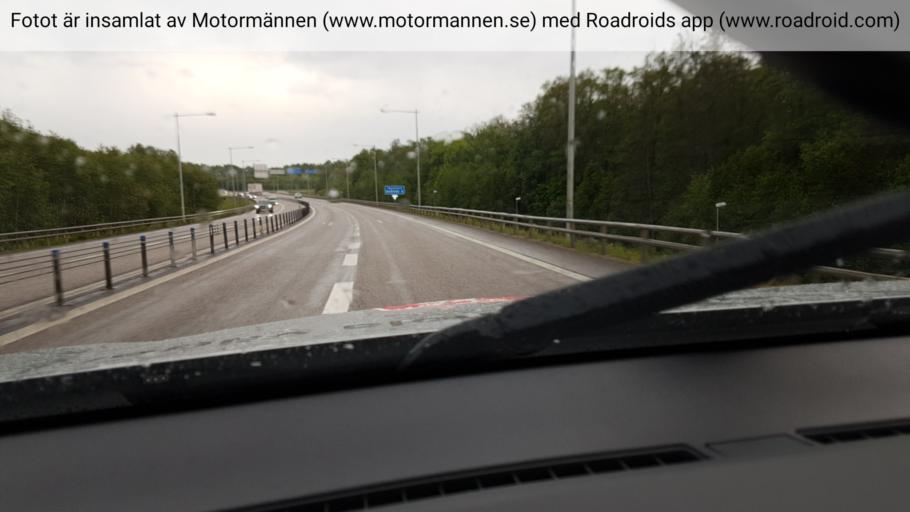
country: SE
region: Vaestra Goetaland
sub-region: Skovde Kommun
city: Skoevde
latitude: 58.3731
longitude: 13.8556
